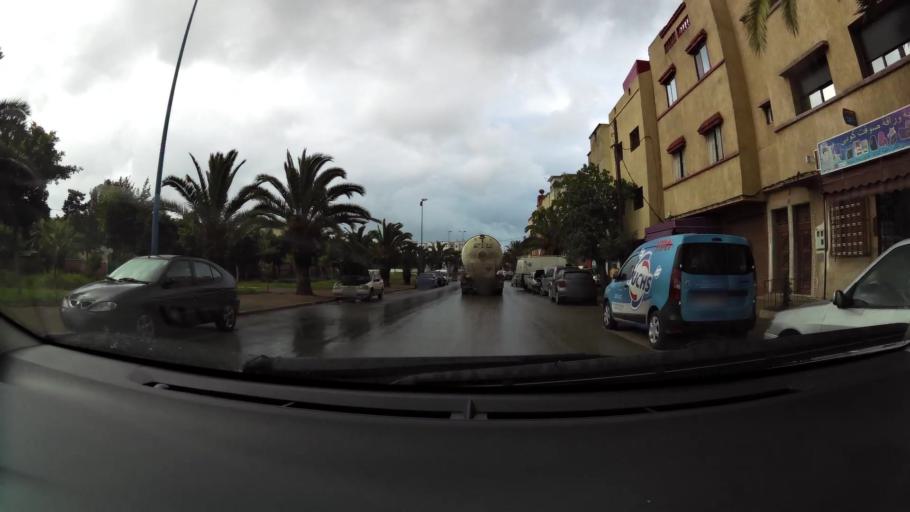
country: MA
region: Grand Casablanca
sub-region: Mohammedia
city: Mohammedia
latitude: 33.6756
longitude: -7.3965
